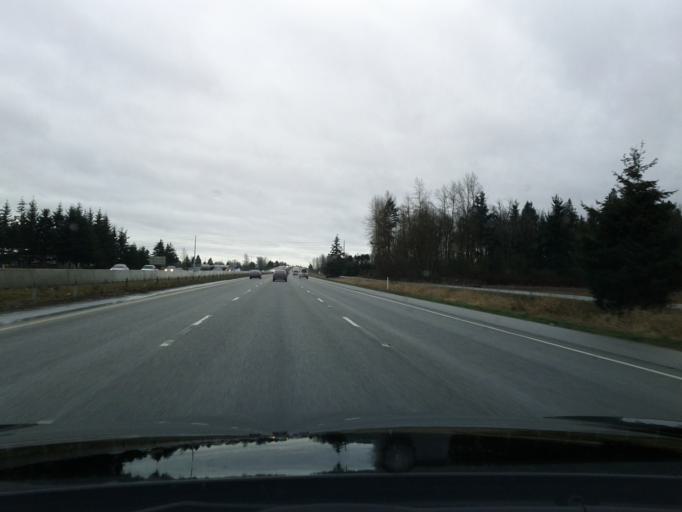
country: US
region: Washington
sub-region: Snohomish County
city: Smokey Point
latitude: 48.1361
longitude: -122.1862
